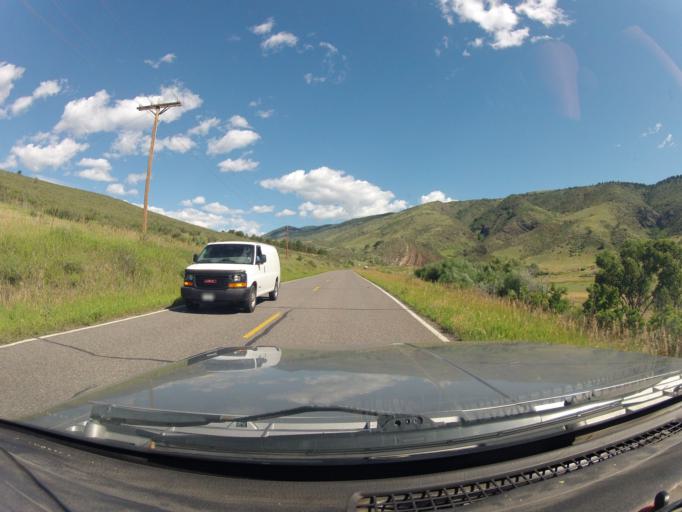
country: US
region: Colorado
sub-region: Larimer County
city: Laporte
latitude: 40.5046
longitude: -105.2282
